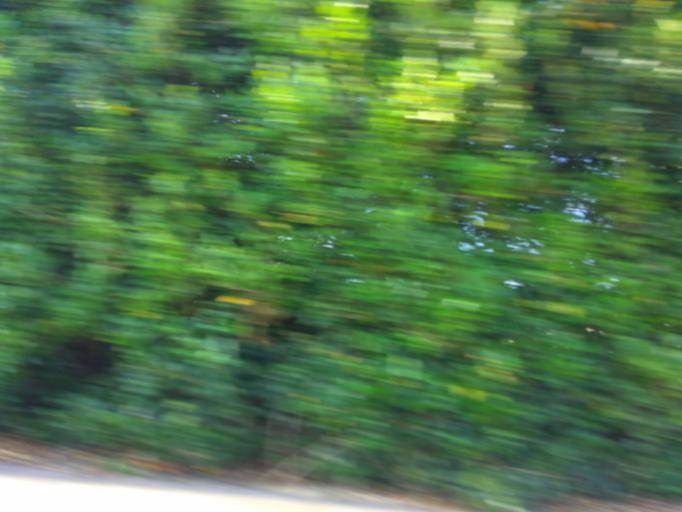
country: TW
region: Taiwan
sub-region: Hsinchu
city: Zhubei
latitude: 24.9787
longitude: 121.0568
